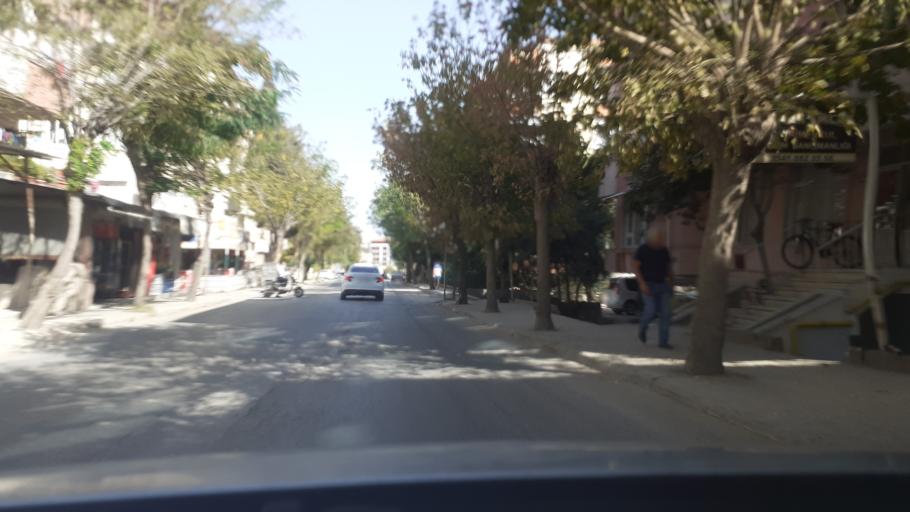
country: TR
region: Hatay
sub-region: Antakya Ilcesi
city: Antakya
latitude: 36.2113
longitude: 36.1543
